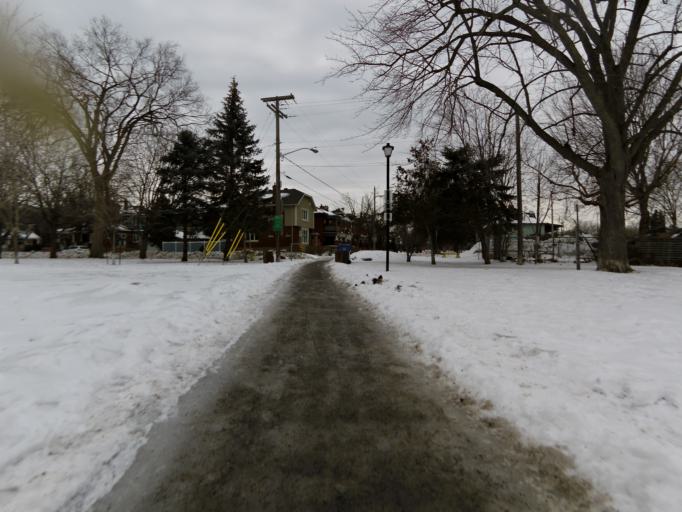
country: CA
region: Ontario
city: Ottawa
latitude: 45.3885
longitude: -75.6879
